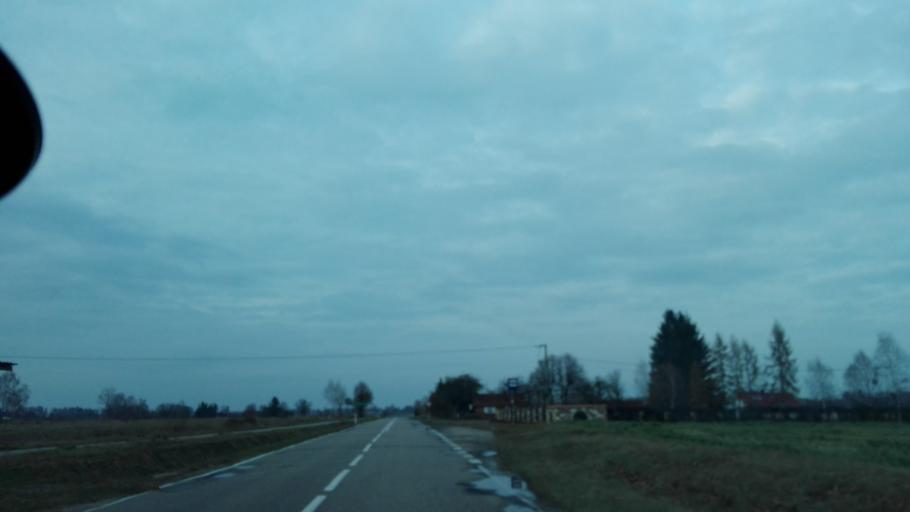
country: PL
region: Lublin Voivodeship
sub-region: Powiat bialski
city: Slawatycze
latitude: 51.6710
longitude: 23.5124
